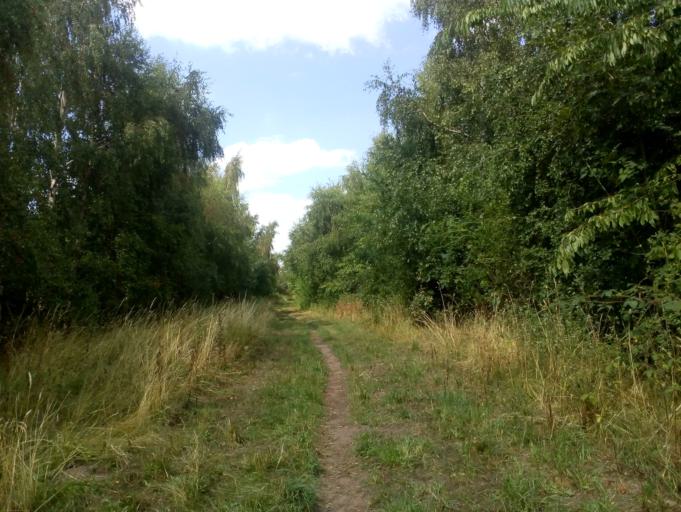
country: GB
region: England
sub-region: North Yorkshire
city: Hambleton
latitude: 53.7646
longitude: -1.1400
